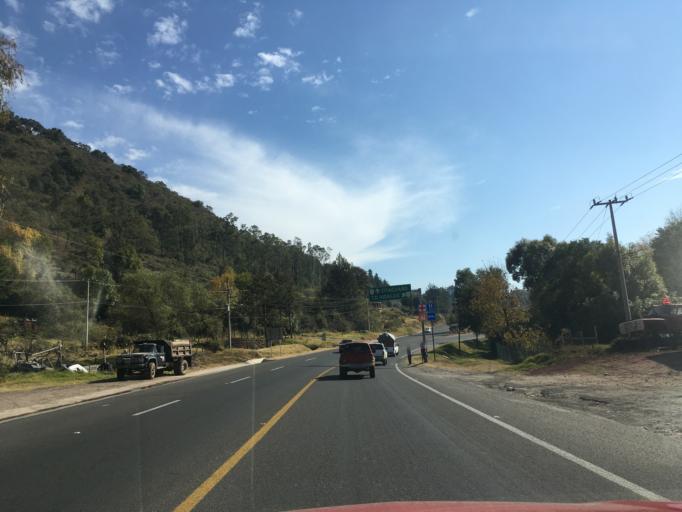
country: MX
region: Michoacan
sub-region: Hidalgo
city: Colonia Ecologica Asociacion de Lucha Social (Lucha Social)
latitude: 19.6997
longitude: -100.5916
